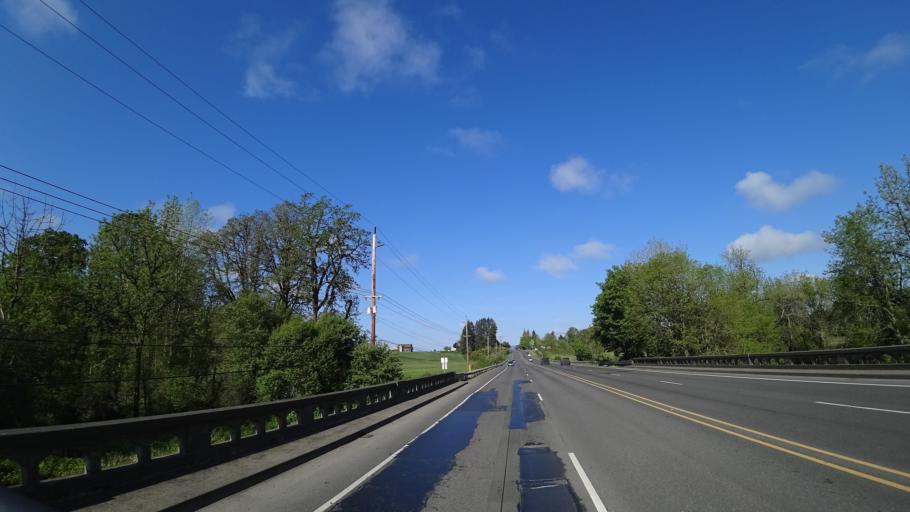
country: US
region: Oregon
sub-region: Washington County
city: Hillsboro
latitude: 45.5199
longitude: -123.0112
